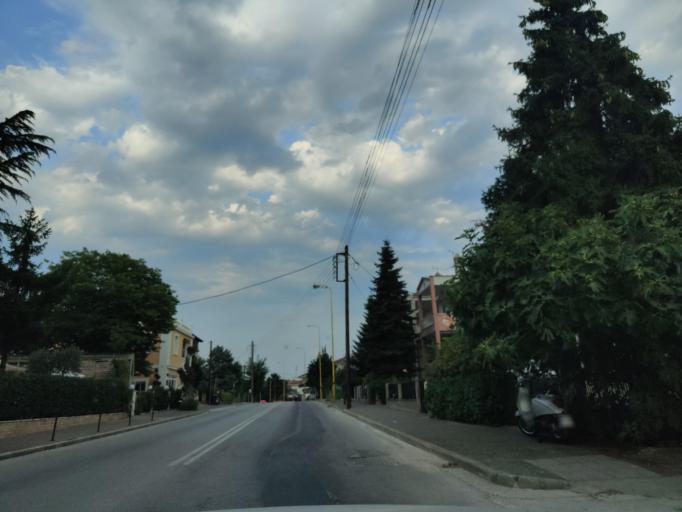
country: GR
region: East Macedonia and Thrace
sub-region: Nomos Dramas
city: Drama
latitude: 41.1530
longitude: 24.1274
